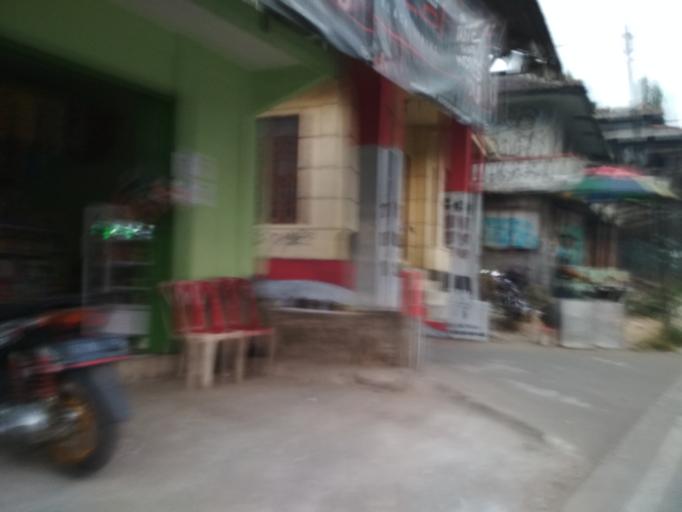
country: ID
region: West Java
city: Caringin
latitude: -6.6685
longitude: 106.8465
